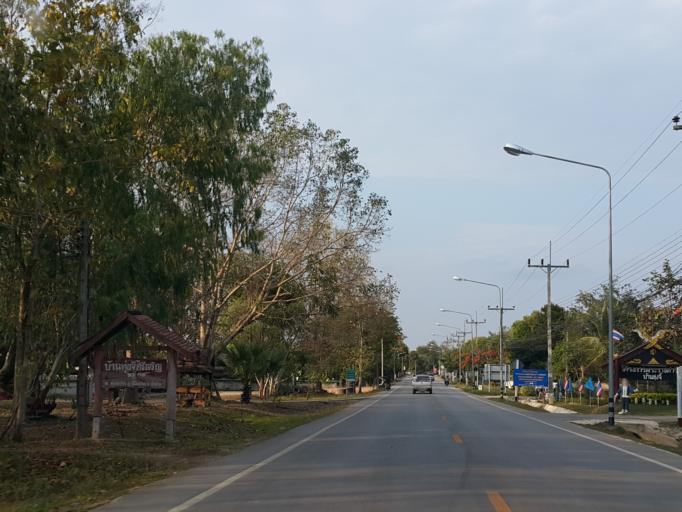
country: TH
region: Lampang
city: Chae Hom
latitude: 18.5354
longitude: 99.4785
